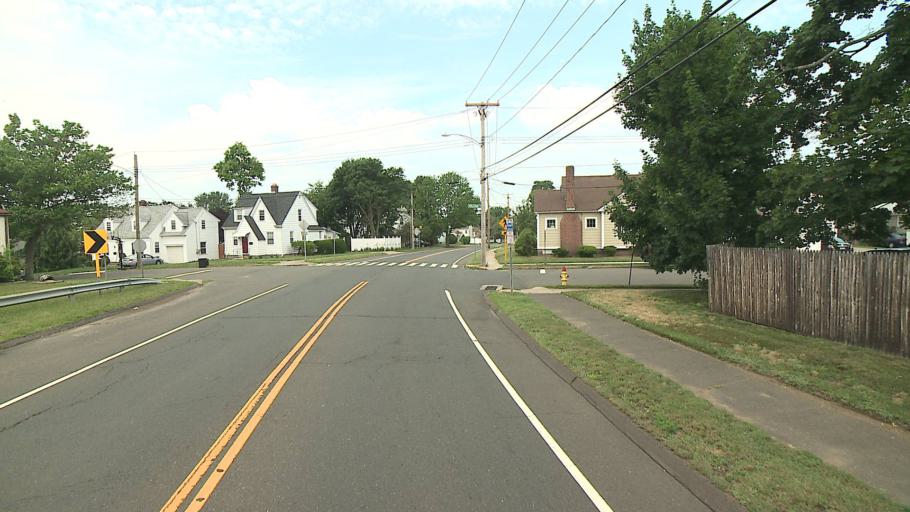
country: US
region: Connecticut
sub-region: New Haven County
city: Woodmont
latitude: 41.2347
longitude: -72.9766
